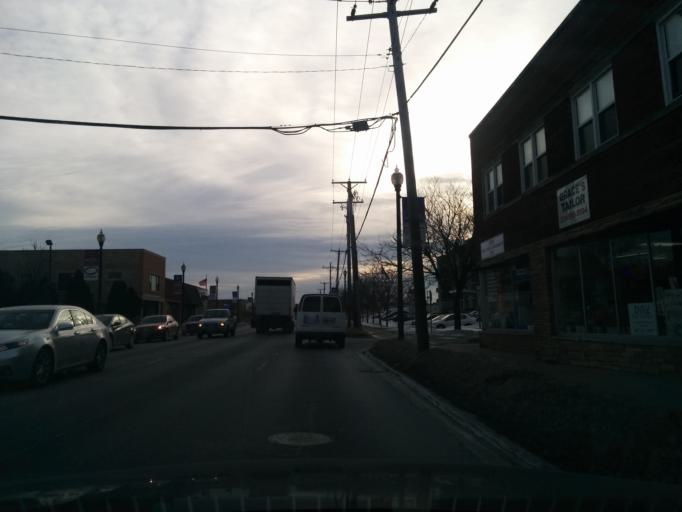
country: US
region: Illinois
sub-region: Cook County
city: Schiller Park
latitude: 41.9544
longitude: -87.8631
